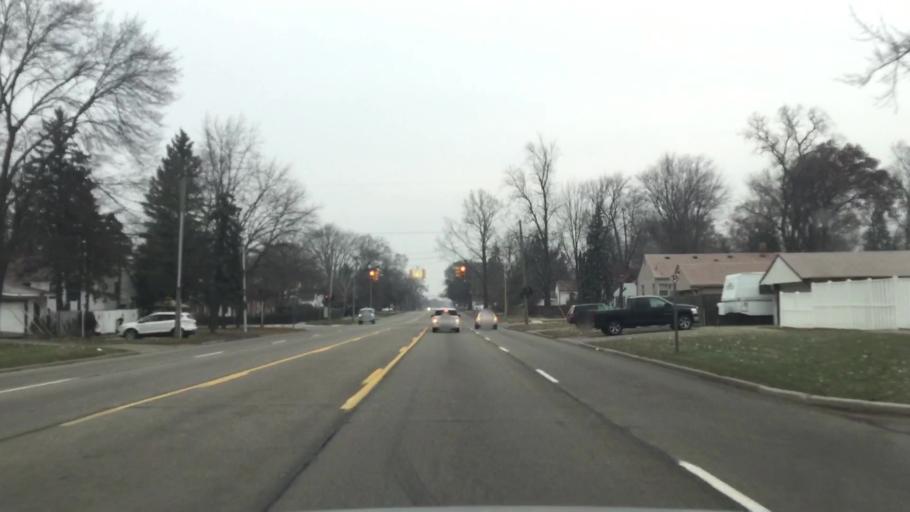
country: US
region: Michigan
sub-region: Wayne County
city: Garden City
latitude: 42.3170
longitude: -83.3499
